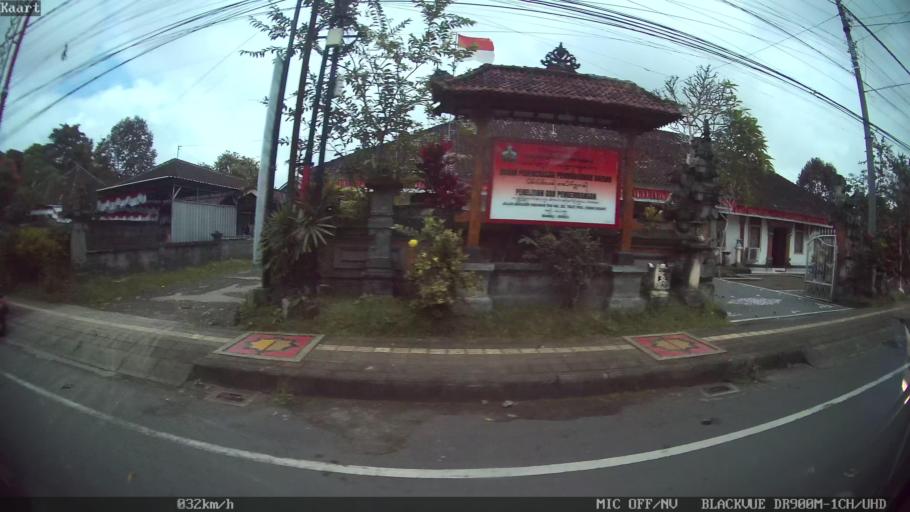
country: ID
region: Bali
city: Bangli
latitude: -8.4608
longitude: 115.3525
